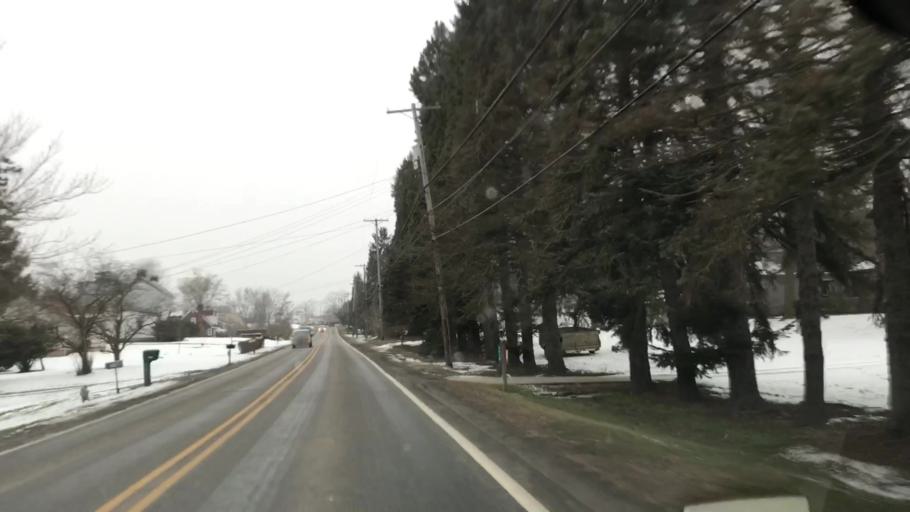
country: US
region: Pennsylvania
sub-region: Beaver County
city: Industry
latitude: 40.7015
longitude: -80.3962
